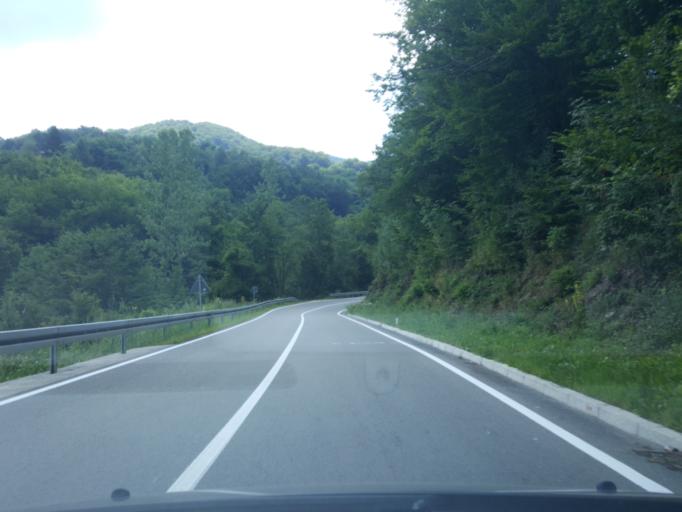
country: RS
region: Central Serbia
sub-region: Moravicki Okrug
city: Gornji Milanovac
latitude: 44.1510
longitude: 20.5049
